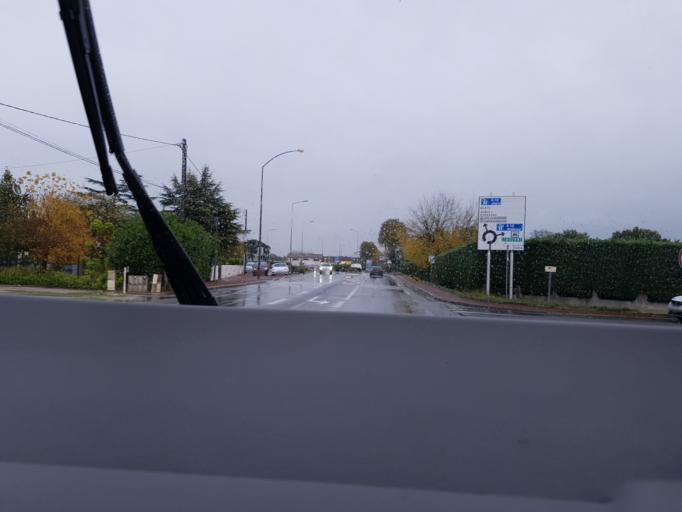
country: FR
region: Aquitaine
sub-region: Departement de la Gironde
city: Cubzac-les-Ponts
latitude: 44.9931
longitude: -0.4355
